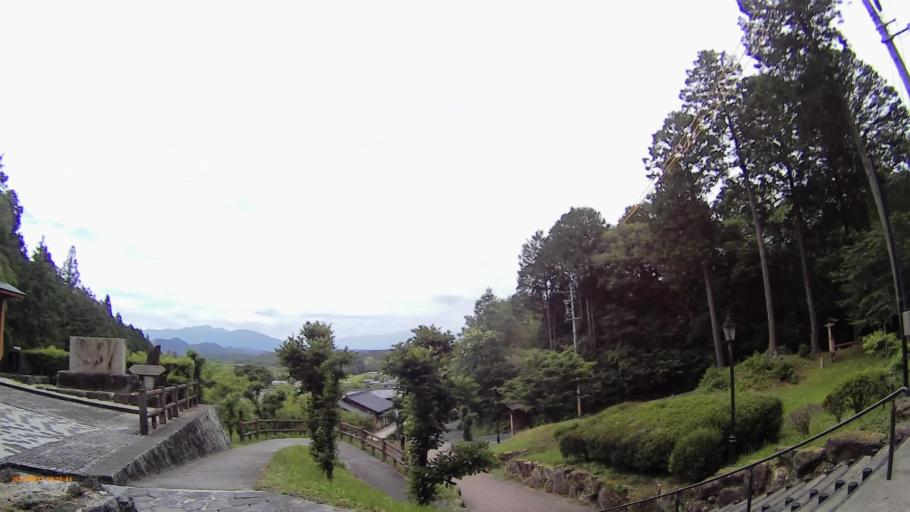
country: JP
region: Gifu
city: Nakatsugawa
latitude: 35.4628
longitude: 137.4229
